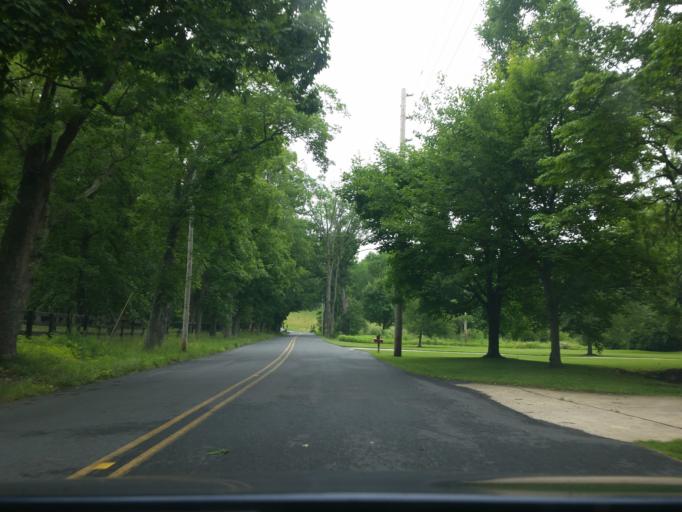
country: US
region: Pennsylvania
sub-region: Dauphin County
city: Skyline View
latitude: 40.4002
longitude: -76.6451
